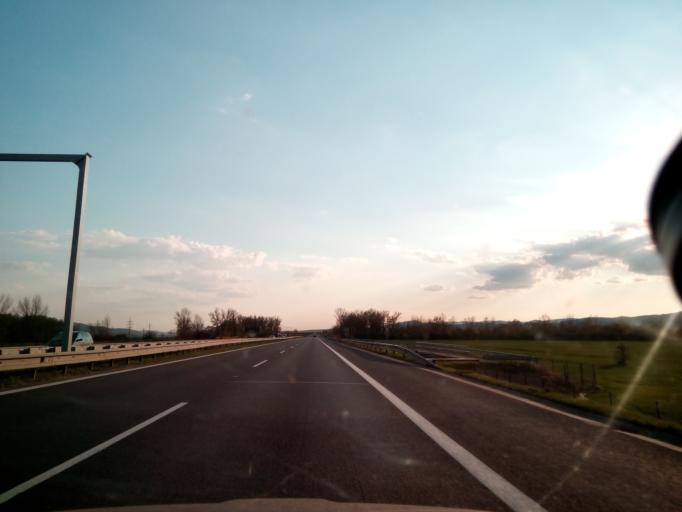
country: SK
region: Nitriansky
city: Dubnica nad Vahom
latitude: 48.9851
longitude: 18.1927
